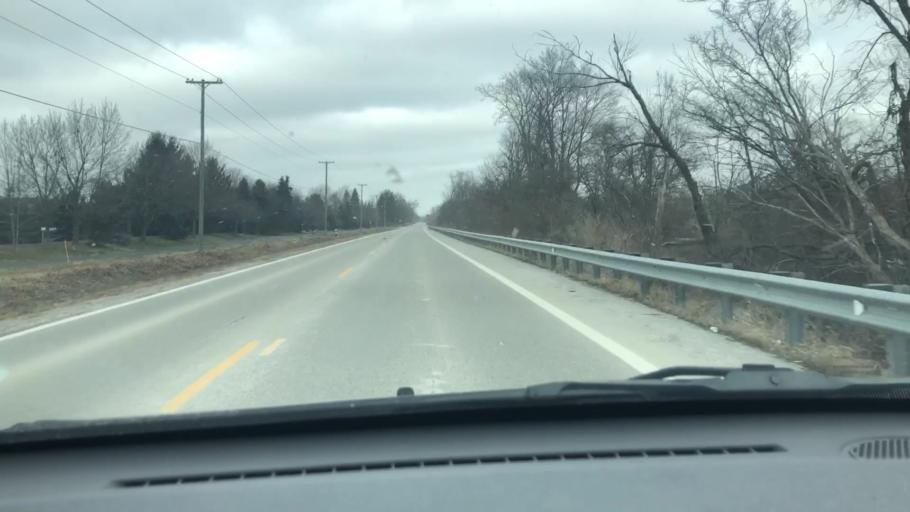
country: US
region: Michigan
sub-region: Macomb County
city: Shelby
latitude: 42.7318
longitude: -83.0171
